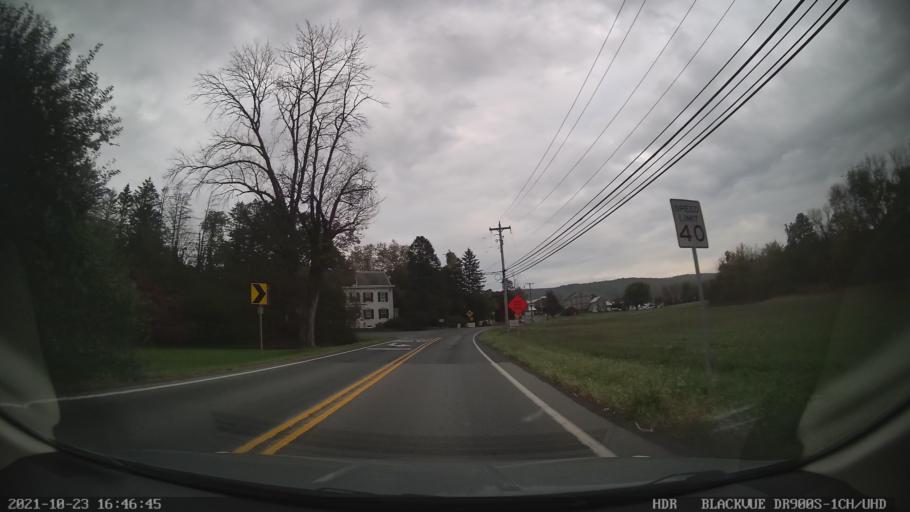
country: US
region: Pennsylvania
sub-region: Berks County
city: Red Lion
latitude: 40.4923
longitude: -75.6460
